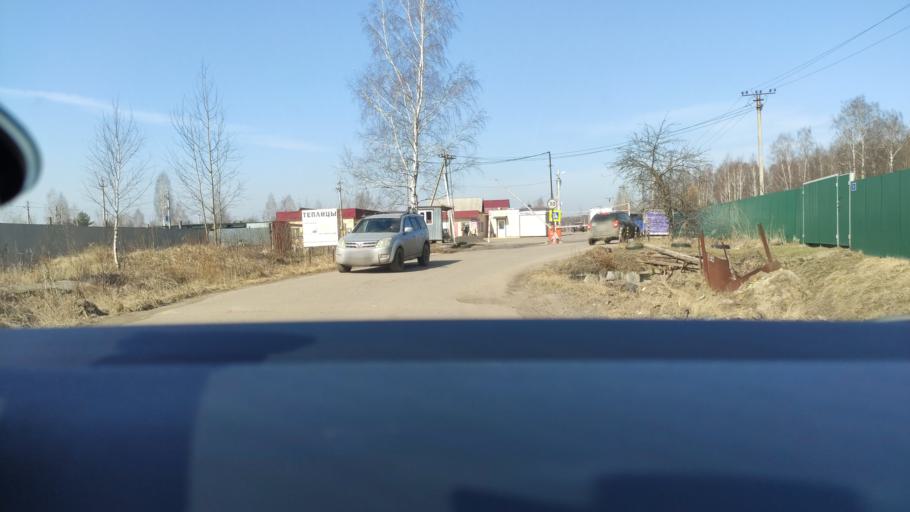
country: RU
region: Moskovskaya
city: Imeni Vorovskogo
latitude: 55.7766
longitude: 38.3736
